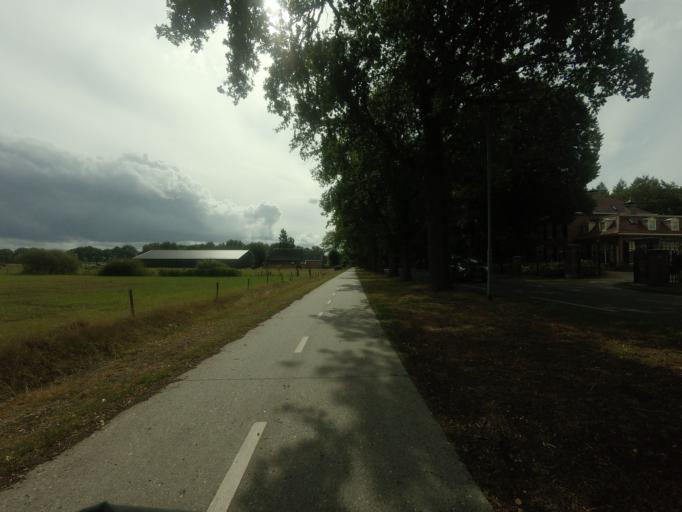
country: NL
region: Drenthe
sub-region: Gemeente Assen
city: Assen
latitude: 53.0499
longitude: 6.4564
